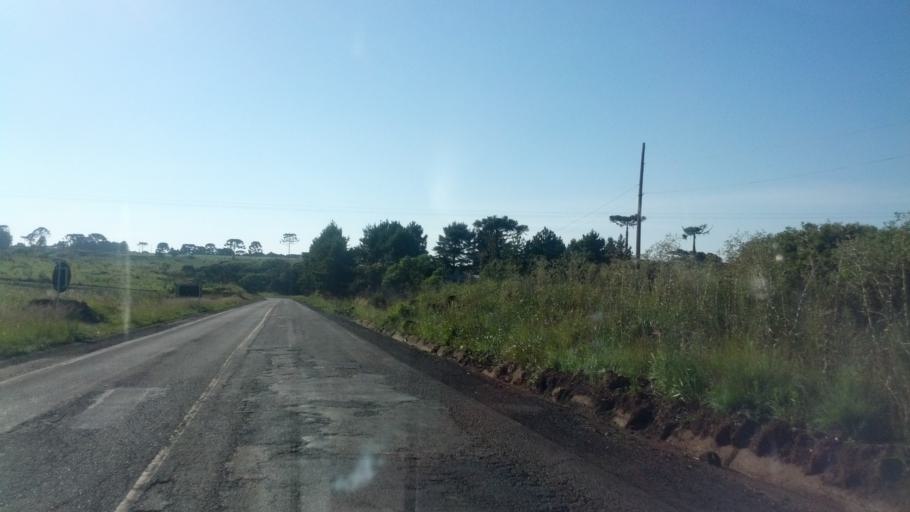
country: BR
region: Santa Catarina
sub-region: Lages
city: Lages
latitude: -27.9483
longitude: -50.5033
